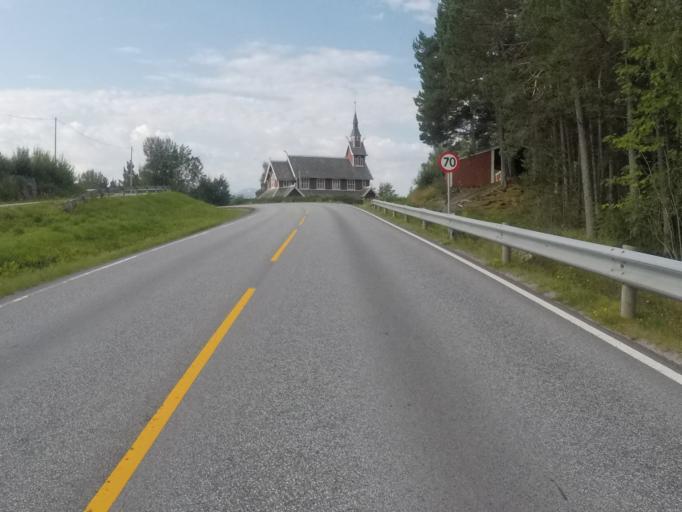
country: NO
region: More og Romsdal
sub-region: Molde
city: Hjelset
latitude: 62.6867
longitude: 7.4555
